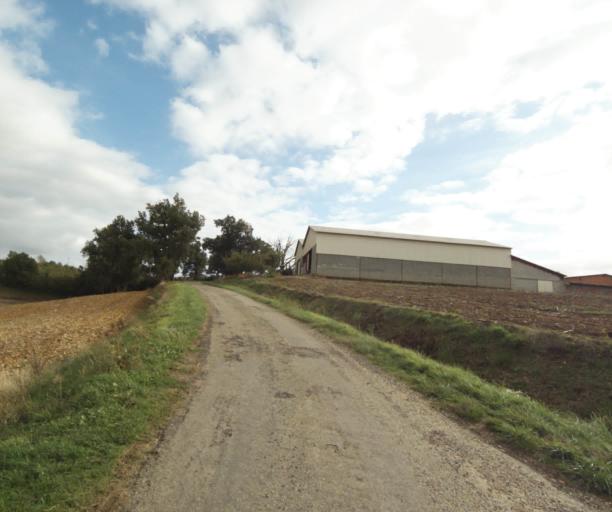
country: FR
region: Midi-Pyrenees
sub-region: Departement du Tarn-et-Garonne
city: Beaumont-de-Lomagne
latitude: 43.9091
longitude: 1.0943
